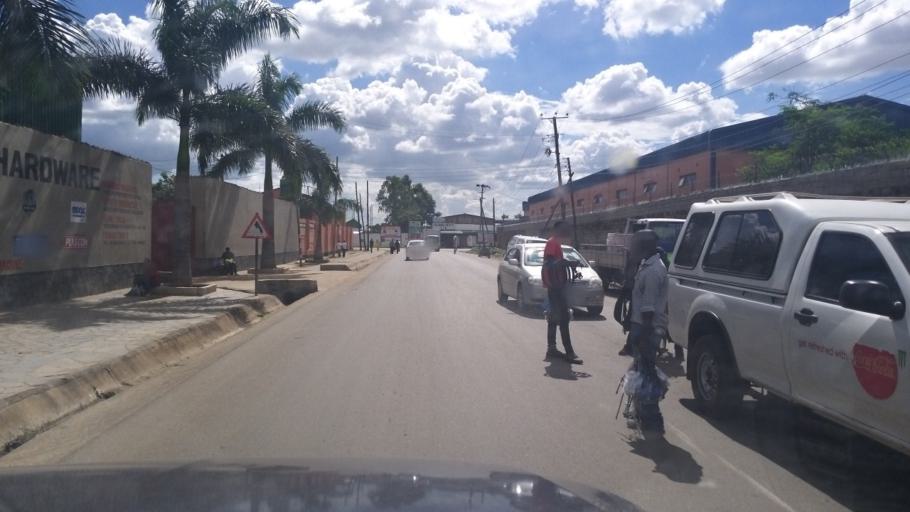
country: ZM
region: Lusaka
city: Lusaka
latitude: -15.4122
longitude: 28.2756
